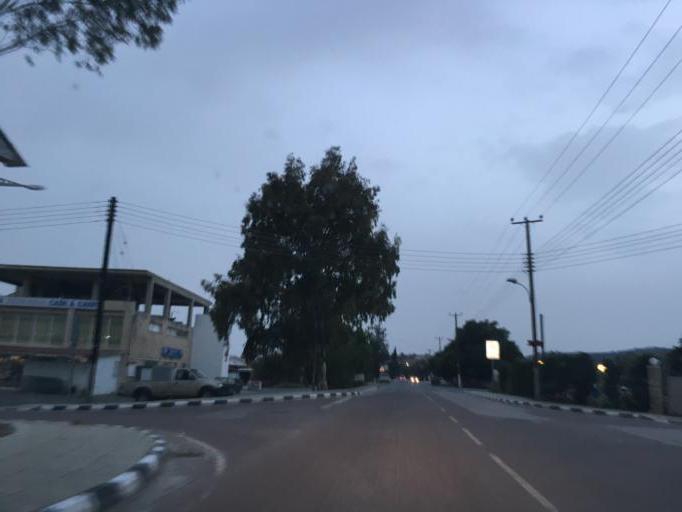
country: CY
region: Limassol
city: Parekklisha
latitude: 34.7474
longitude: 33.1588
